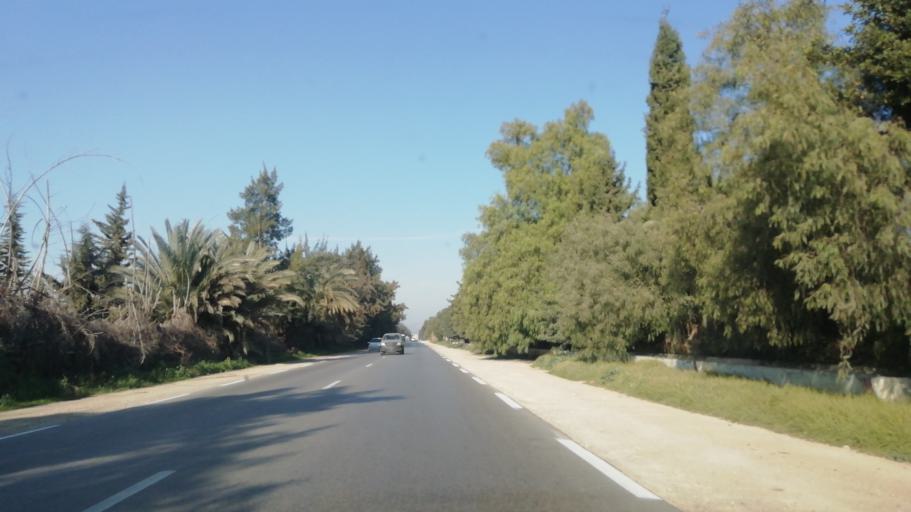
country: DZ
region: Relizane
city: Relizane
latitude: 35.7276
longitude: 0.4774
